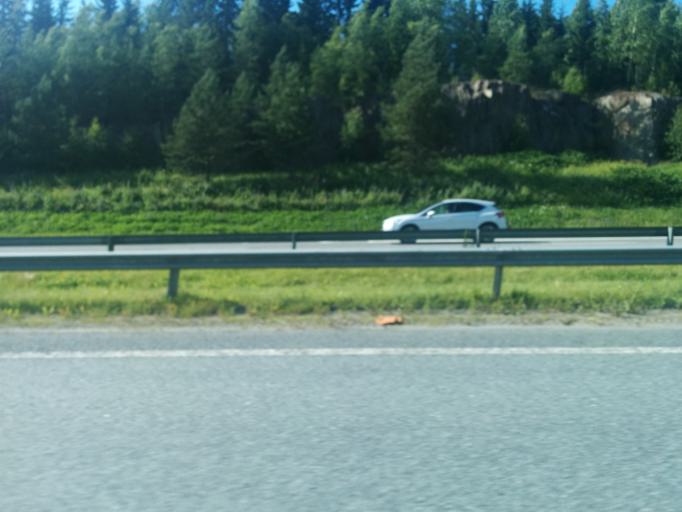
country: FI
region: Pirkanmaa
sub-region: Tampere
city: Tampere
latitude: 61.5000
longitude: 23.8893
